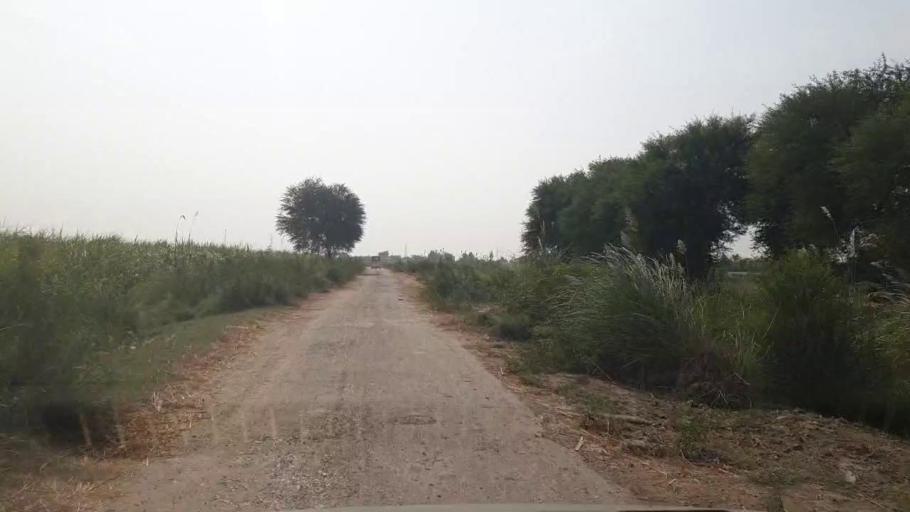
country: PK
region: Sindh
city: Tando Muhammad Khan
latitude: 25.1189
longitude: 68.3875
